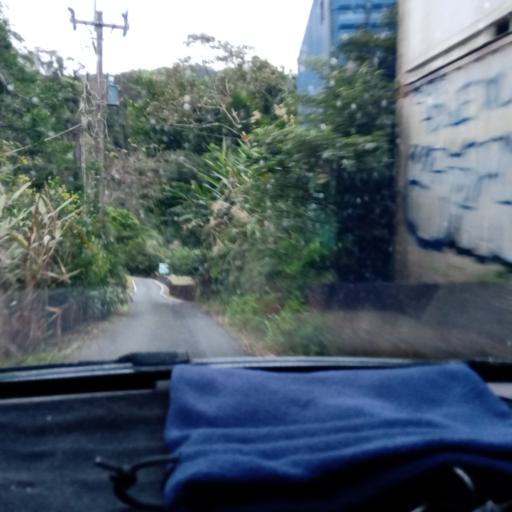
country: TW
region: Taiwan
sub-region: Yilan
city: Yilan
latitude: 24.8102
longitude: 121.7032
